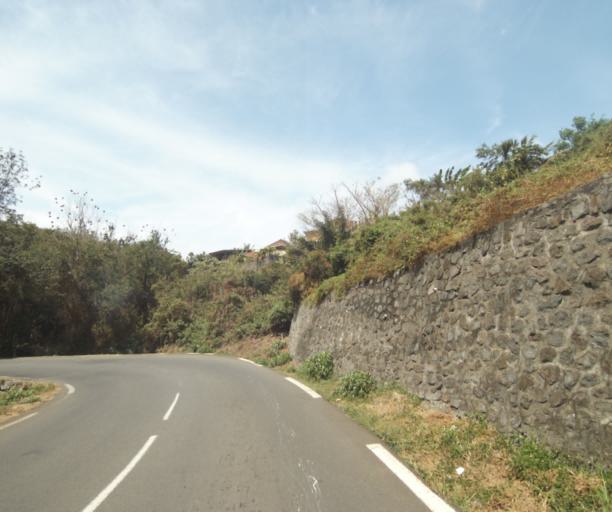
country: RE
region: Reunion
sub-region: Reunion
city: Trois-Bassins
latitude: -21.0985
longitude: 55.2715
